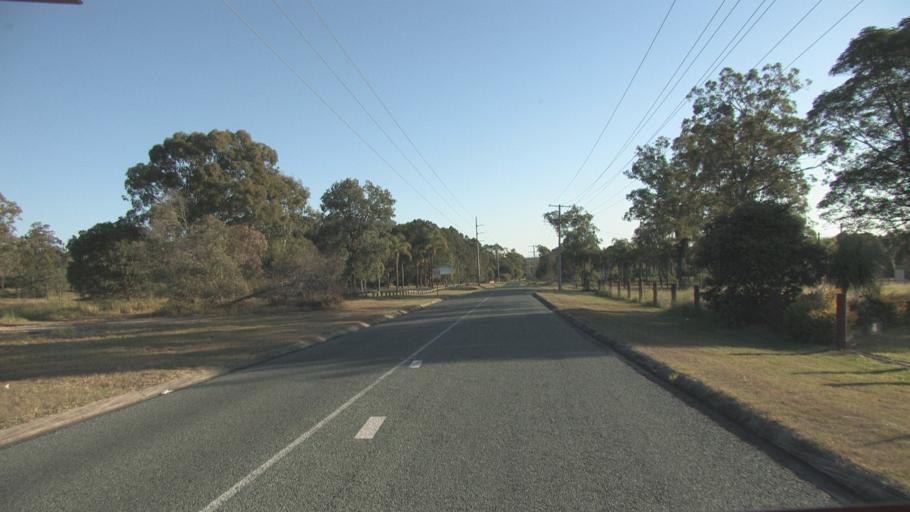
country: AU
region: Queensland
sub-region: Logan
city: Logan Reserve
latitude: -27.7247
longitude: 153.1041
